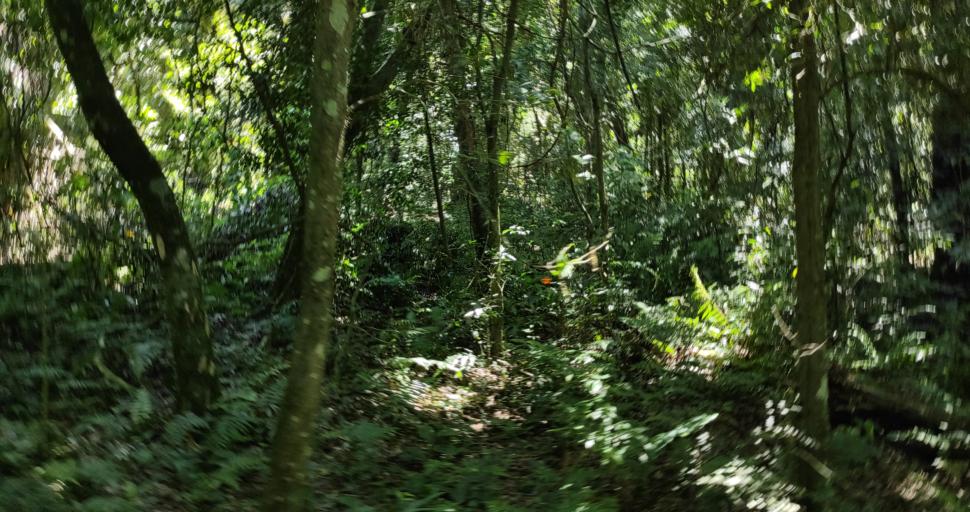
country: BR
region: Rio Grande do Sul
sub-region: Tres Passos
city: Tres Passos
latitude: -27.1473
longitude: -53.8967
